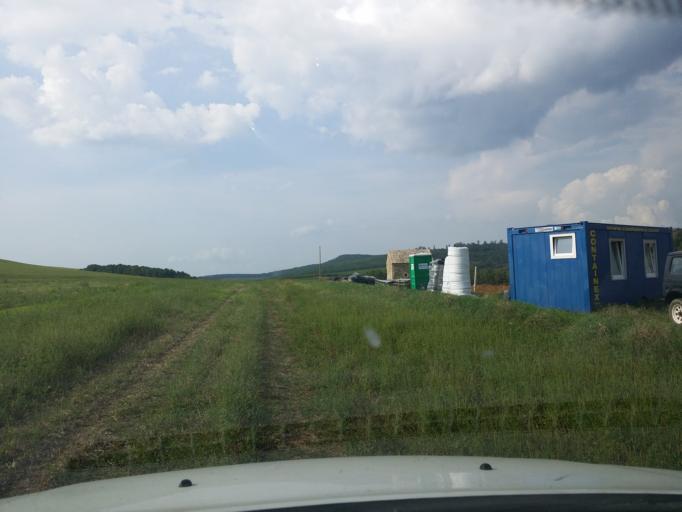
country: HU
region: Nograd
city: Rimoc
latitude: 47.9786
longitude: 19.4617
